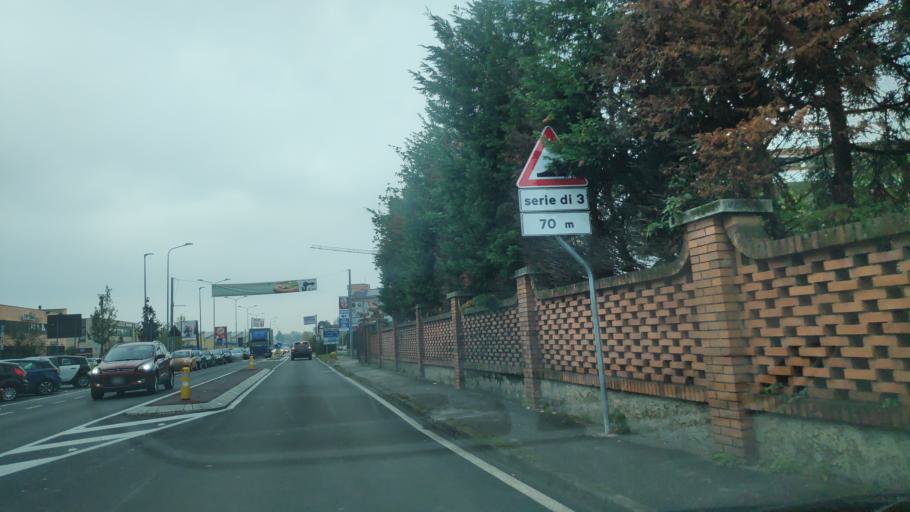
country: IT
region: Lombardy
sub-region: Citta metropolitana di Milano
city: Rozzano
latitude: 45.3748
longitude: 9.1691
